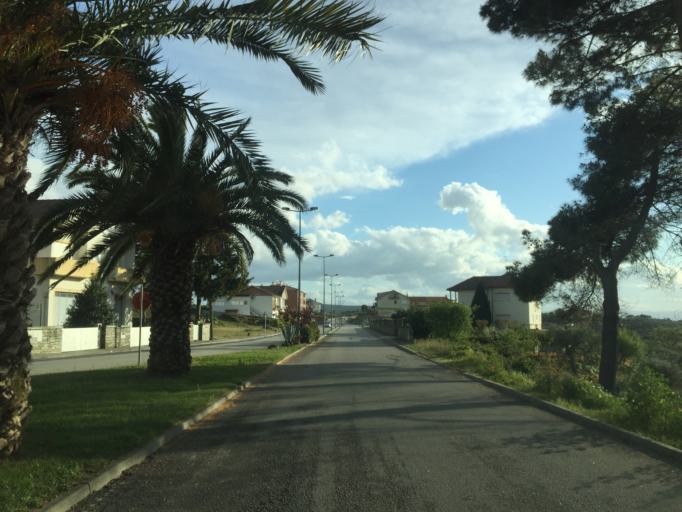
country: PT
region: Braganca
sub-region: Alfandega da Fe
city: Alfandega da Fe
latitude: 41.3375
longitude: -6.9624
